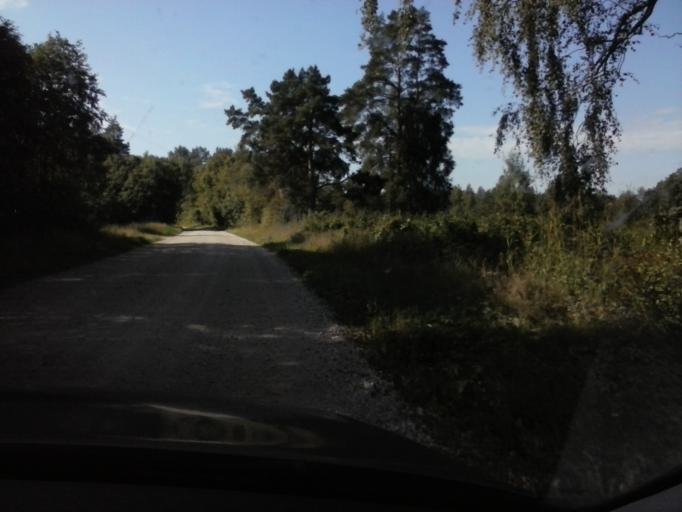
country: EE
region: Laeaene
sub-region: Haapsalu linn
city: Haapsalu
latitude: 58.8791
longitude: 23.5590
